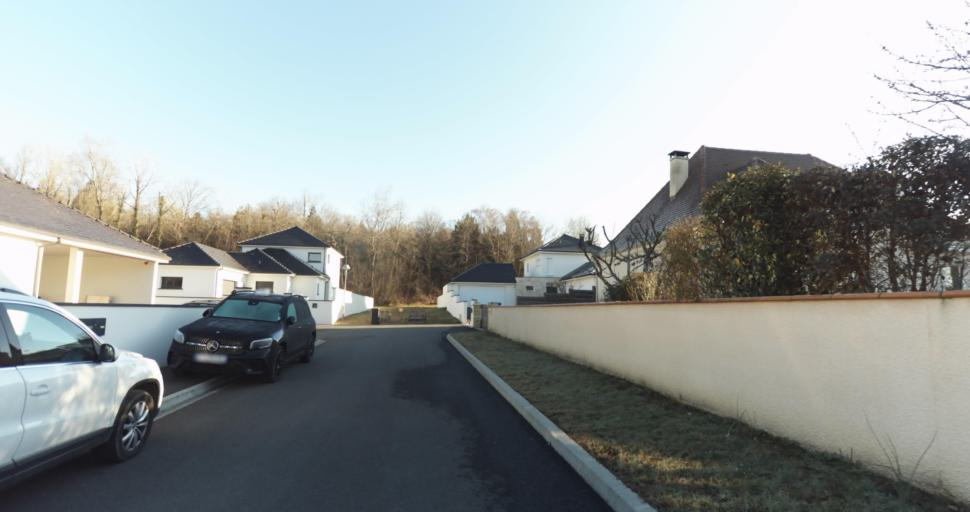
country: FR
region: Aquitaine
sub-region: Departement des Pyrenees-Atlantiques
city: Morlaas
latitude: 43.3298
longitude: -0.2820
